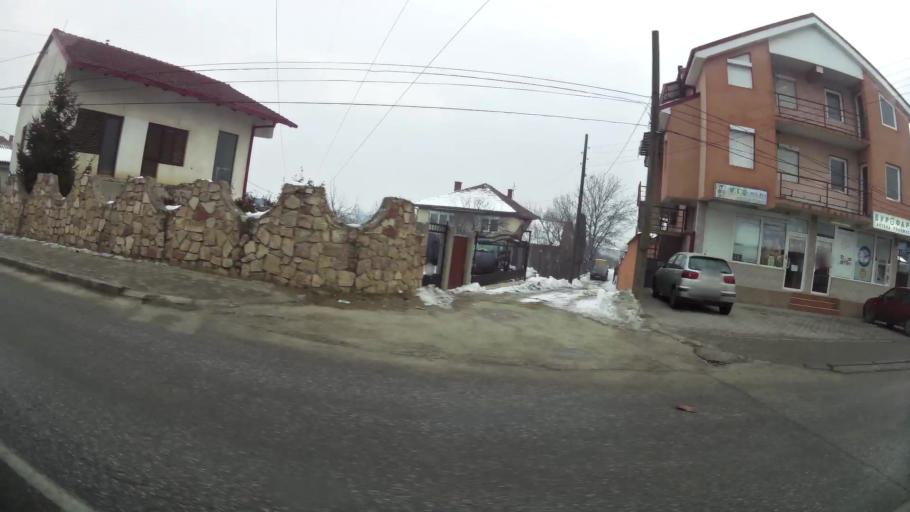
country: MK
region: Saraj
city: Saraj
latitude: 42.0381
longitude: 21.3487
